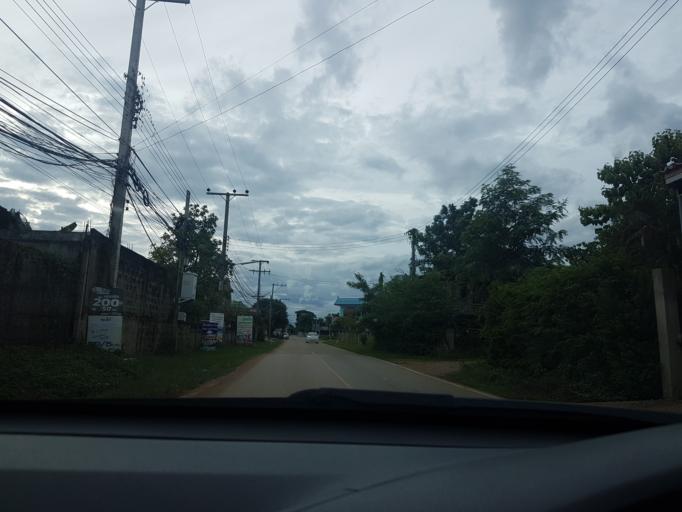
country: TH
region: Lampang
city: Ko Kha
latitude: 18.2104
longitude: 99.4171
